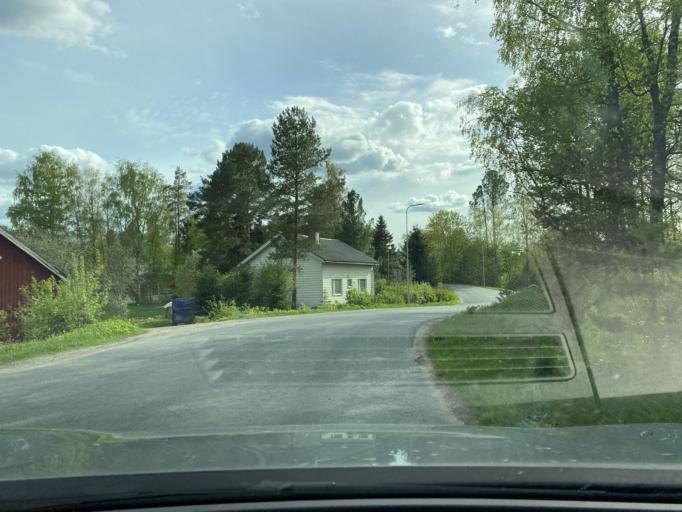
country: FI
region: Varsinais-Suomi
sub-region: Salo
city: Kiikala
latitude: 60.4596
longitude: 23.5507
